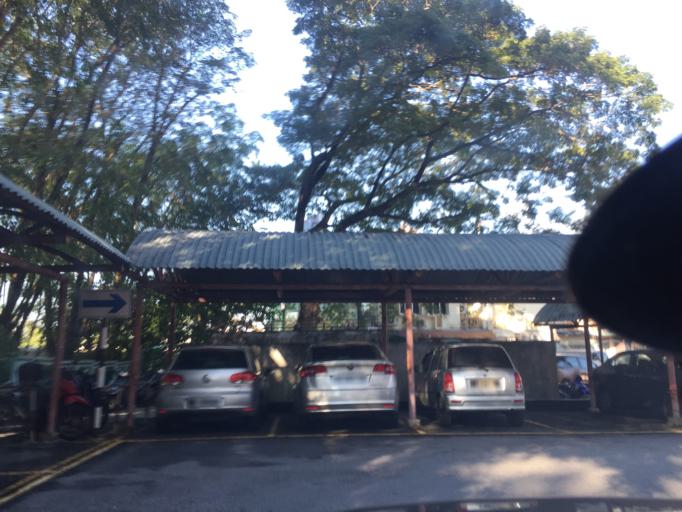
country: MY
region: Kuala Lumpur
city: Kuala Lumpur
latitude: 3.2066
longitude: 101.7361
